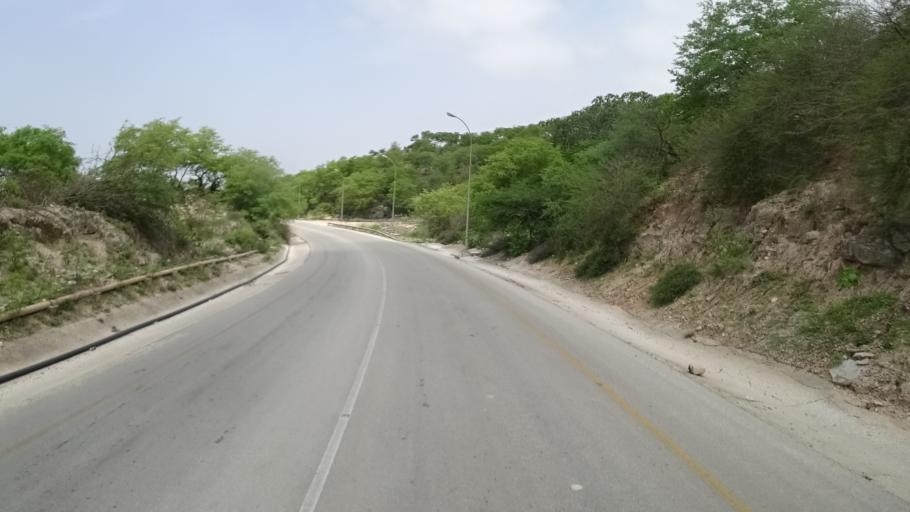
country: OM
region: Zufar
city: Salalah
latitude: 17.0730
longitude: 54.4497
